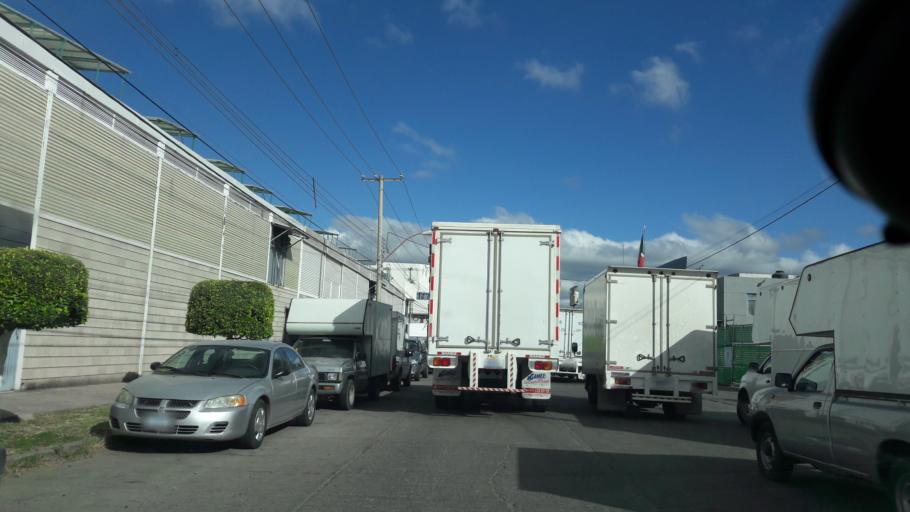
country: MX
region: Guanajuato
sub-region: Leon
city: Medina
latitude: 21.1034
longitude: -101.6291
